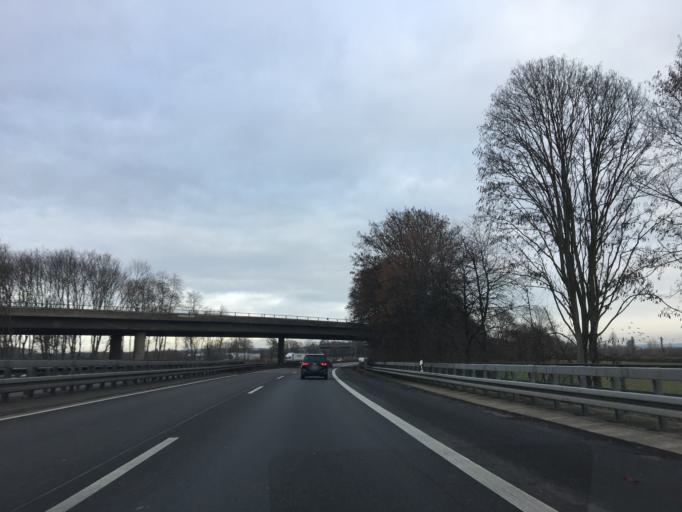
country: DE
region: North Rhine-Westphalia
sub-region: Regierungsbezirk Koln
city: Troisdorf
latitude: 50.7645
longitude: 7.1386
